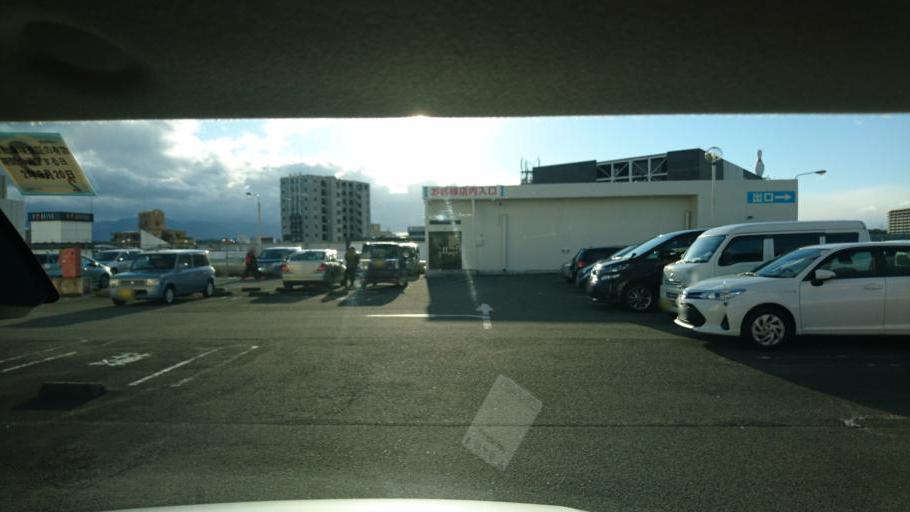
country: JP
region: Miyazaki
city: Miyazaki-shi
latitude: 31.8956
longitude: 131.4194
